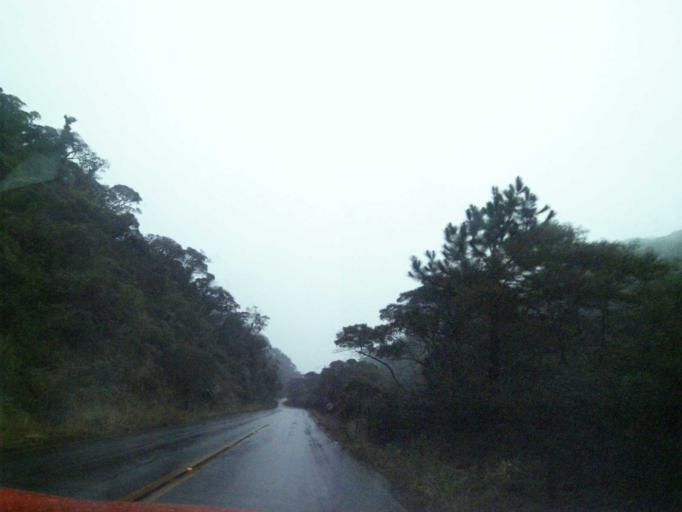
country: BR
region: Santa Catarina
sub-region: Anitapolis
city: Anitapolis
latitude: -27.7628
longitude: -49.0389
